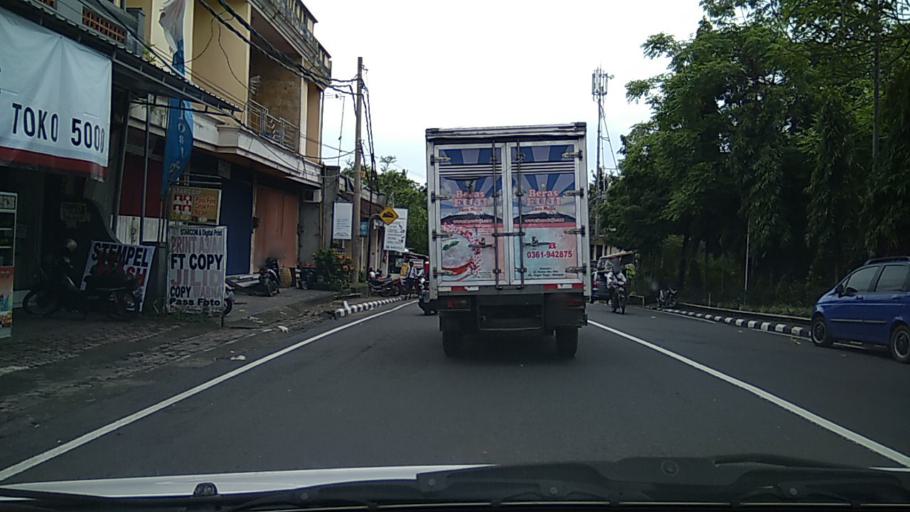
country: ID
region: Bali
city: Banjar Kelodan
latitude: -8.5417
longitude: 115.3328
